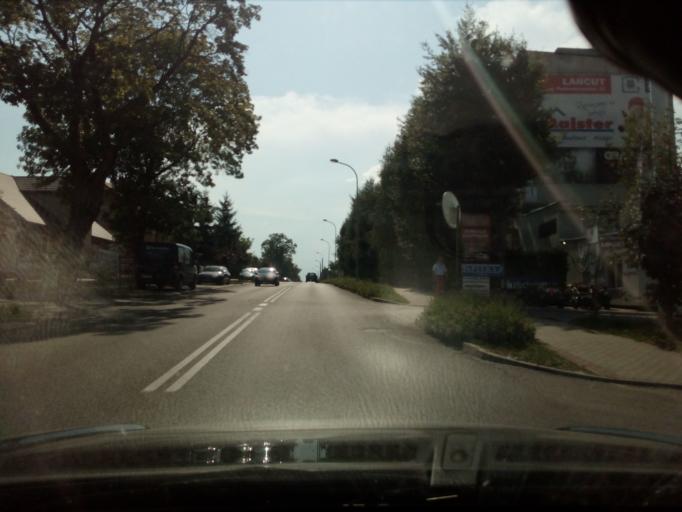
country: PL
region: Subcarpathian Voivodeship
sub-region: Powiat lancucki
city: Lancut
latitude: 50.0644
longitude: 22.2243
